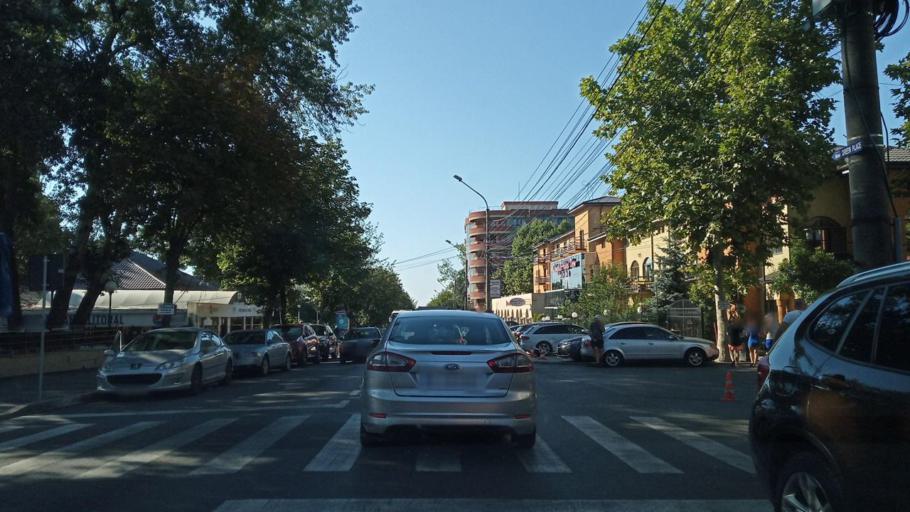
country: RO
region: Constanta
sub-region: Oras Eforie
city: Eforie Nord
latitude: 44.0629
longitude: 28.6349
